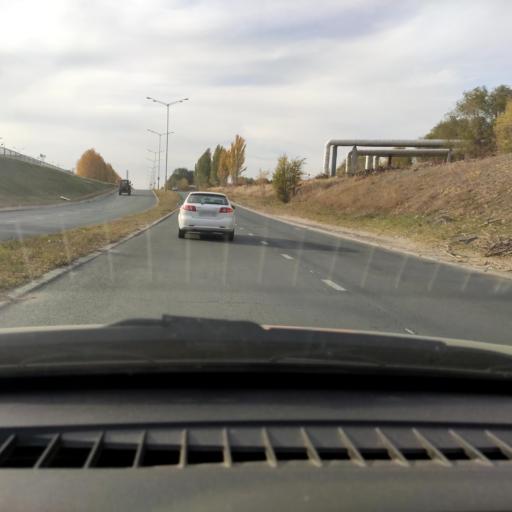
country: RU
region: Samara
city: Tol'yatti
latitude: 53.5671
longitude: 49.2845
